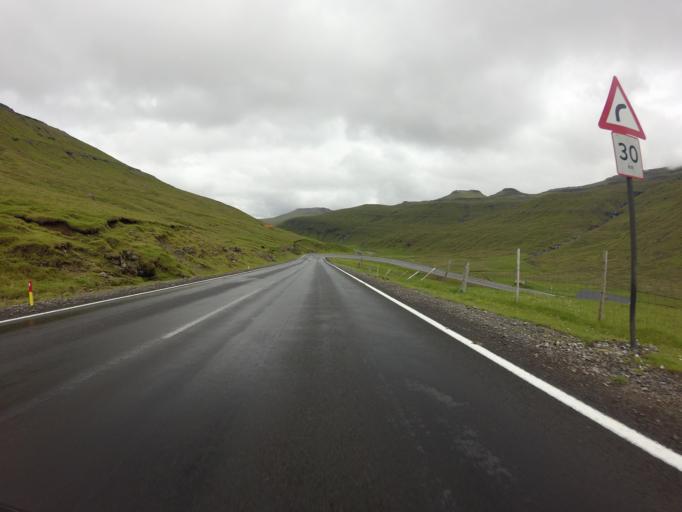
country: FO
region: Streymoy
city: Kollafjordhur
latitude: 62.1188
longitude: -6.9863
